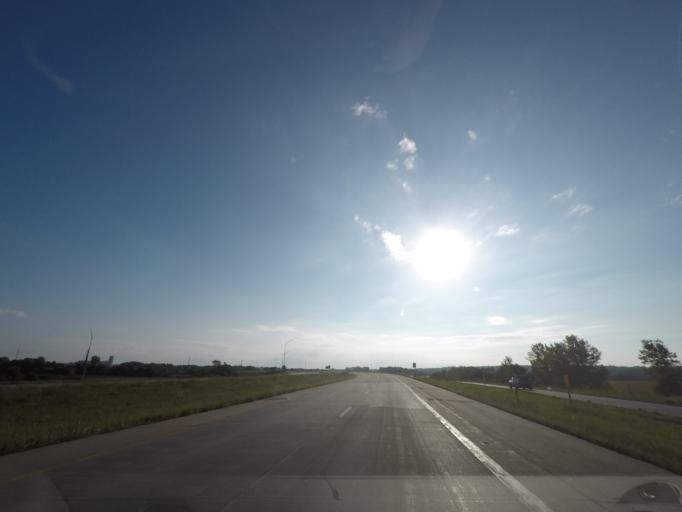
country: US
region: Iowa
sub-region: Warren County
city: Carlisle
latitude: 41.5113
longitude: -93.5294
